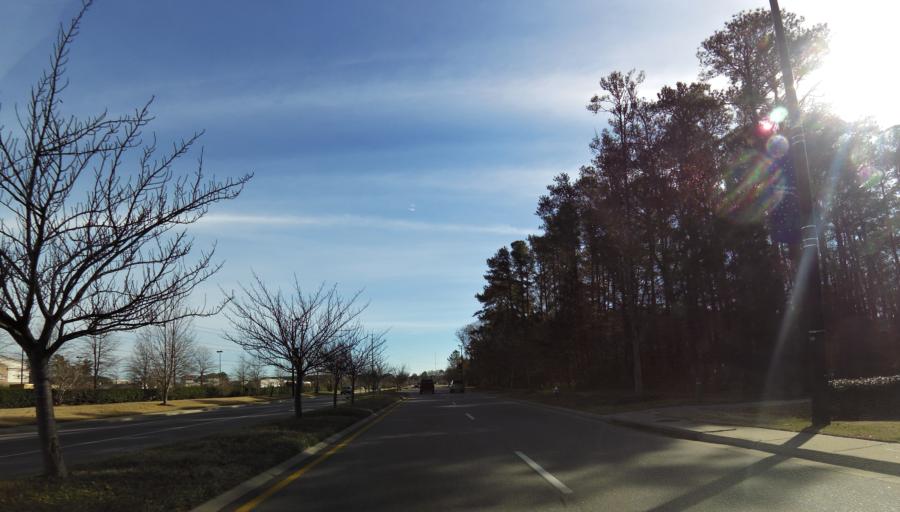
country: US
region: Virginia
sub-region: City of Hampton
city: Hampton
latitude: 37.0360
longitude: -76.3964
